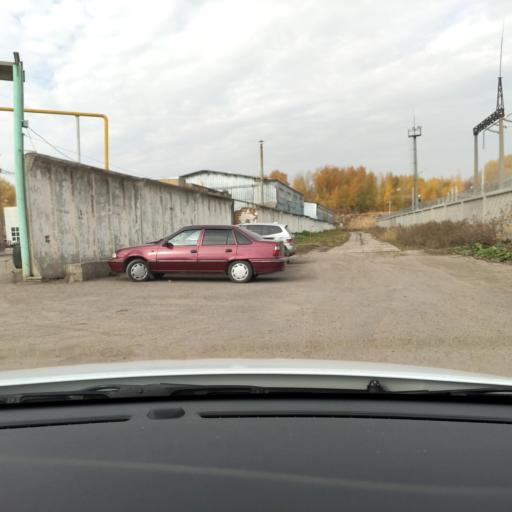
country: RU
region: Tatarstan
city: Verkhniy Uslon
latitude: 55.8040
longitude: 49.0475
